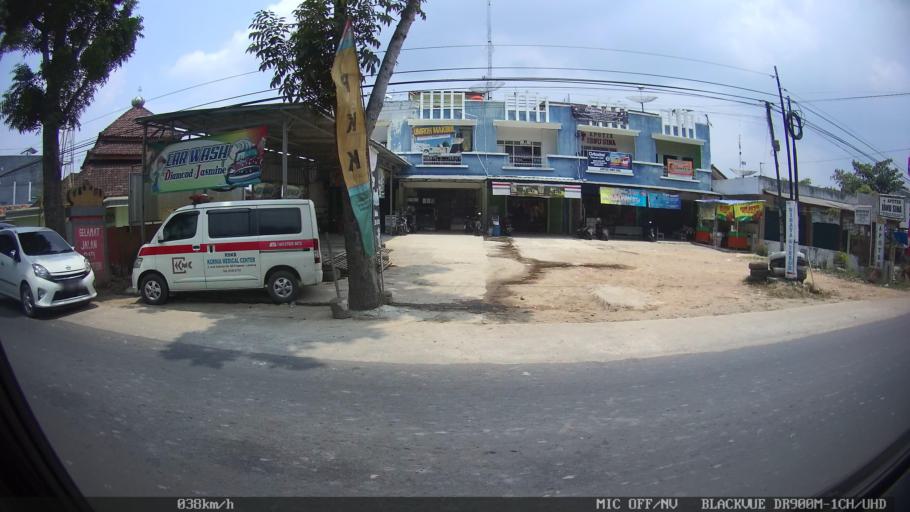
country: ID
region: Lampung
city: Pringsewu
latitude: -5.3556
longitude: 104.9656
